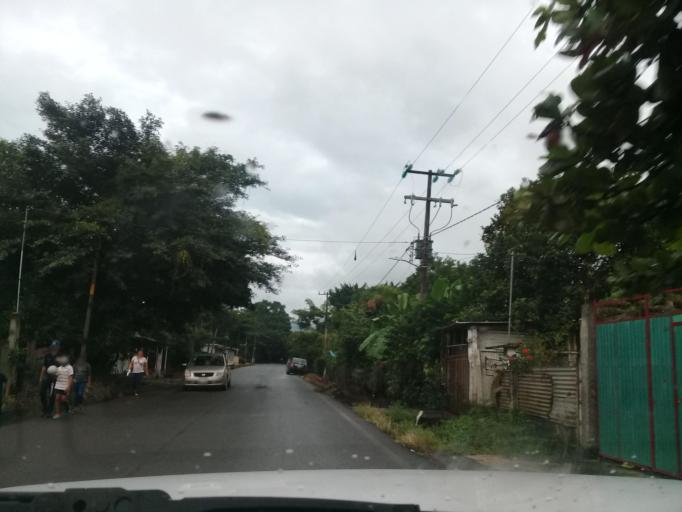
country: MX
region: Veracruz
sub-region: San Andres Tuxtla
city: Cerro las Iguanas
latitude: 18.4220
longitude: -95.2178
